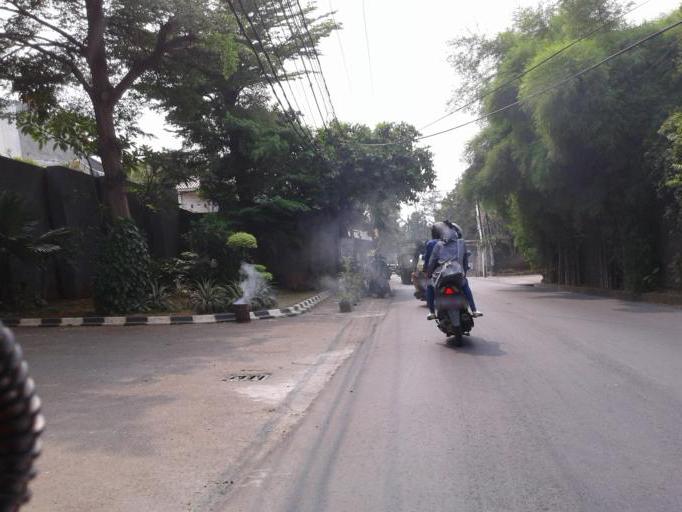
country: ID
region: Banten
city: South Tangerang
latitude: -6.2919
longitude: 106.7451
